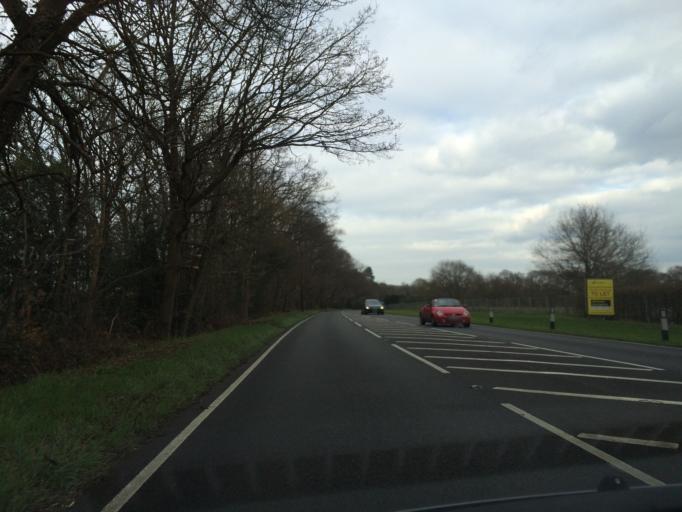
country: GB
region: England
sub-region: Surrey
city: Woking
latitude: 51.3528
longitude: -0.5619
